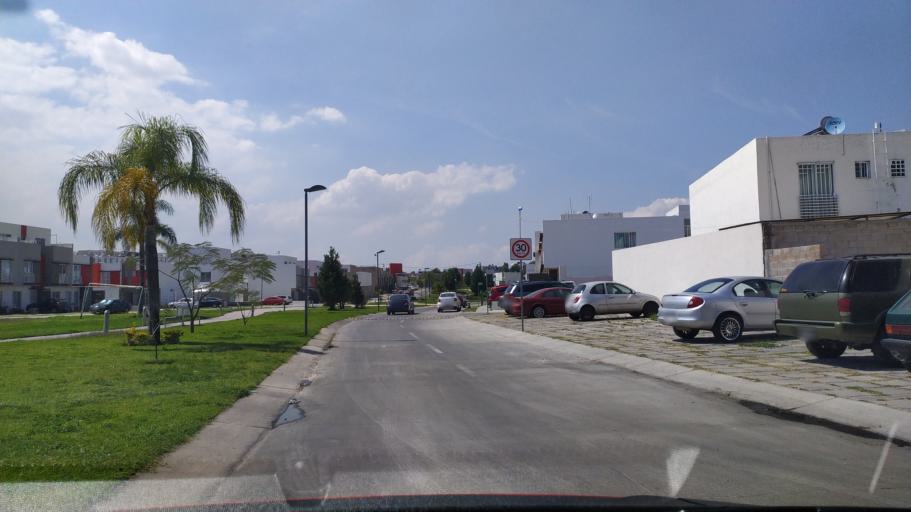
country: MX
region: Jalisco
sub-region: Zapopan
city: Campo Real
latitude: 20.7765
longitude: -103.4307
